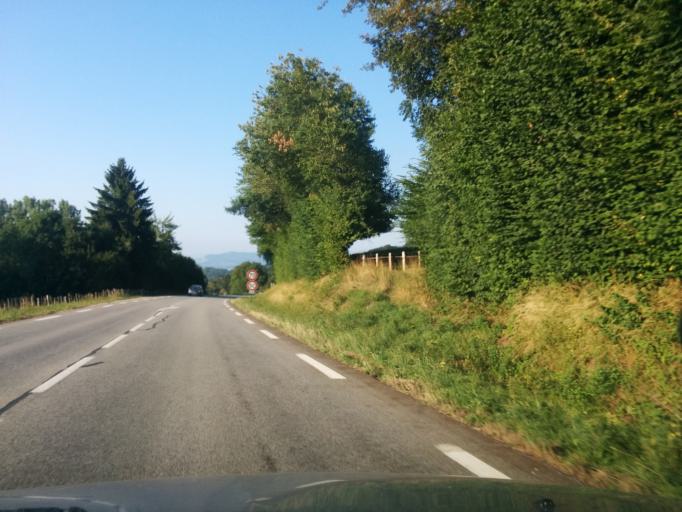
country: FR
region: Rhone-Alpes
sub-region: Departement de l'Isere
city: Montferrat
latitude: 45.4709
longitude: 5.5831
